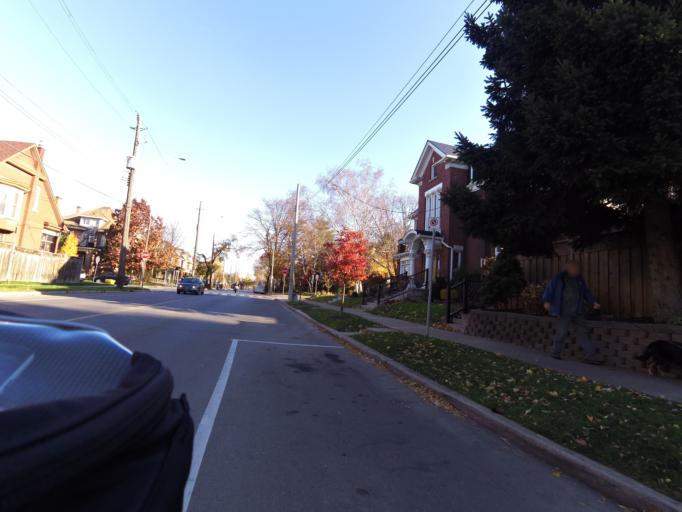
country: CA
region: Ontario
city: Hamilton
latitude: 43.2459
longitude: -79.8398
